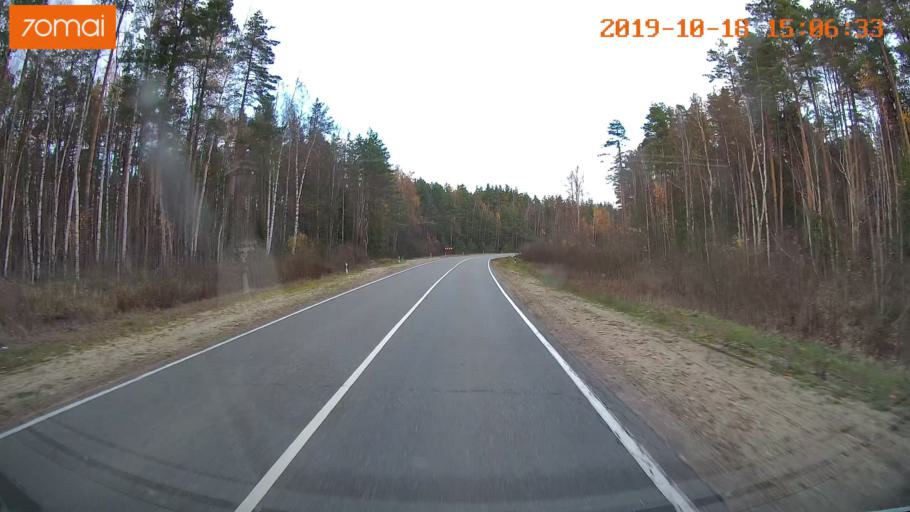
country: RU
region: Vladimir
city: Gus'-Khrustal'nyy
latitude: 55.5319
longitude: 40.5795
